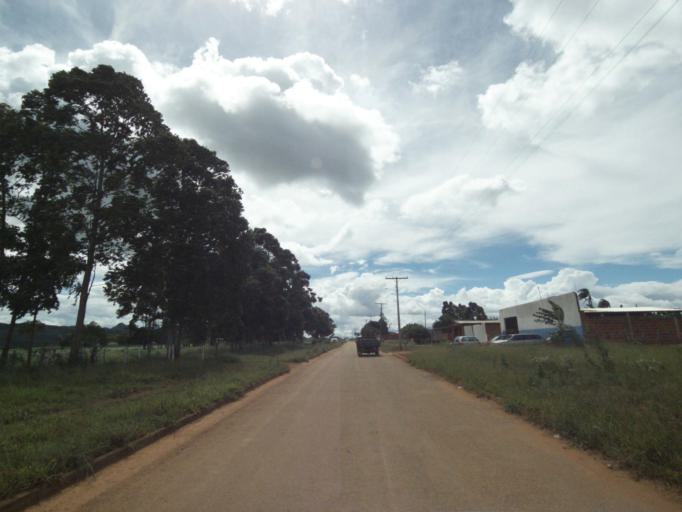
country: BR
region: Goias
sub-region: Pirenopolis
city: Pirenopolis
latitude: -15.7832
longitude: -48.7946
